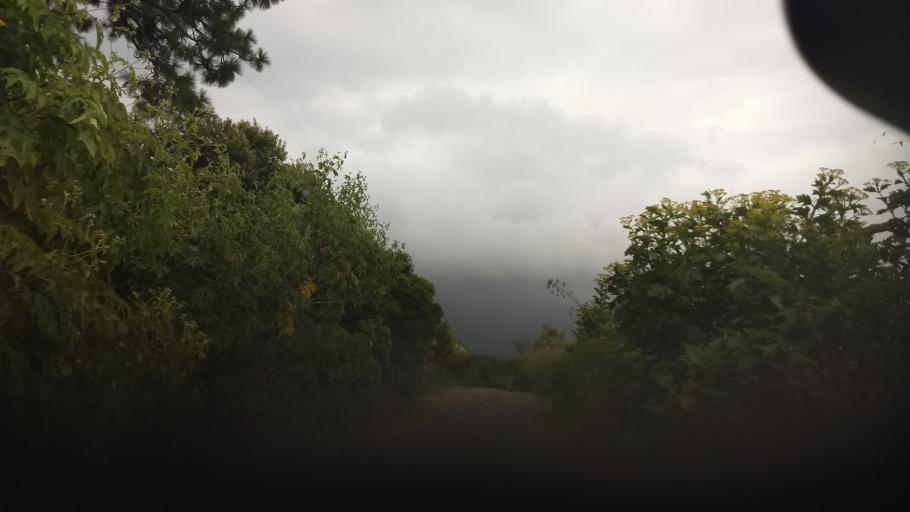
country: MX
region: Jalisco
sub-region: Tonila
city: San Marcos
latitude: 19.4665
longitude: -103.5350
